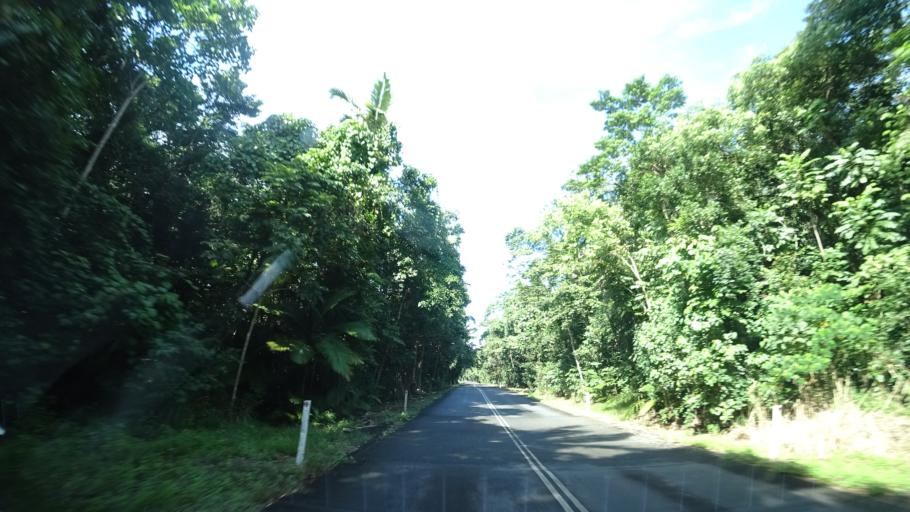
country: AU
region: Queensland
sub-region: Cairns
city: Port Douglas
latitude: -16.1484
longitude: 145.4405
